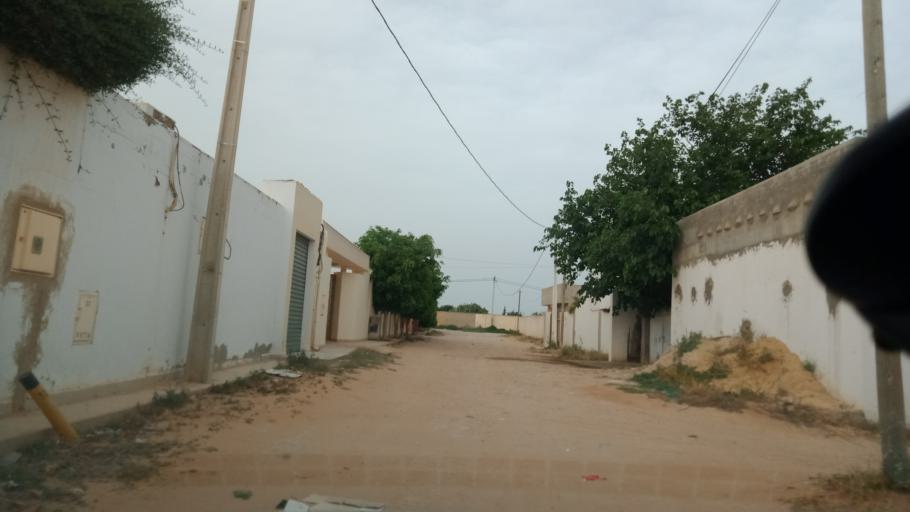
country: TN
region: Safaqis
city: Al Qarmadah
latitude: 34.7869
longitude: 10.7635
